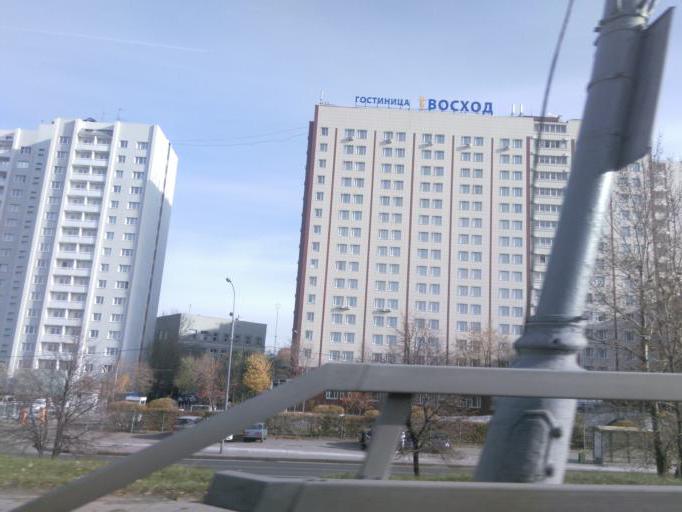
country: RU
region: Moscow
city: Novovladykino
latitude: 55.8496
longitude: 37.5851
